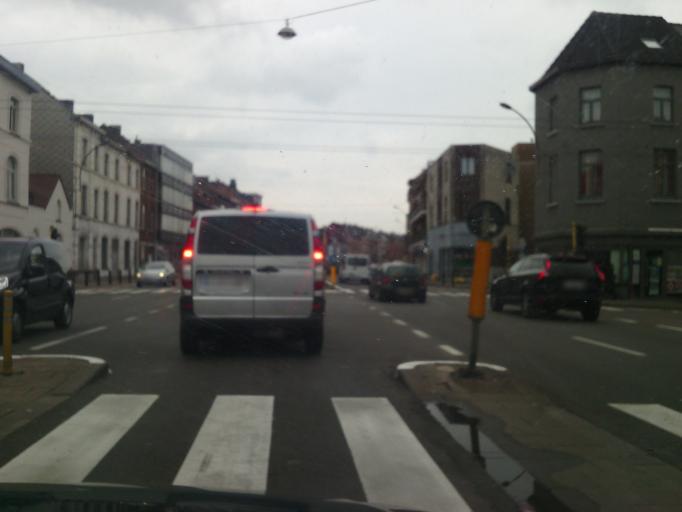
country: BE
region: Flanders
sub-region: Provincie Oost-Vlaanderen
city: Gent
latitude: 51.0635
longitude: 3.6953
